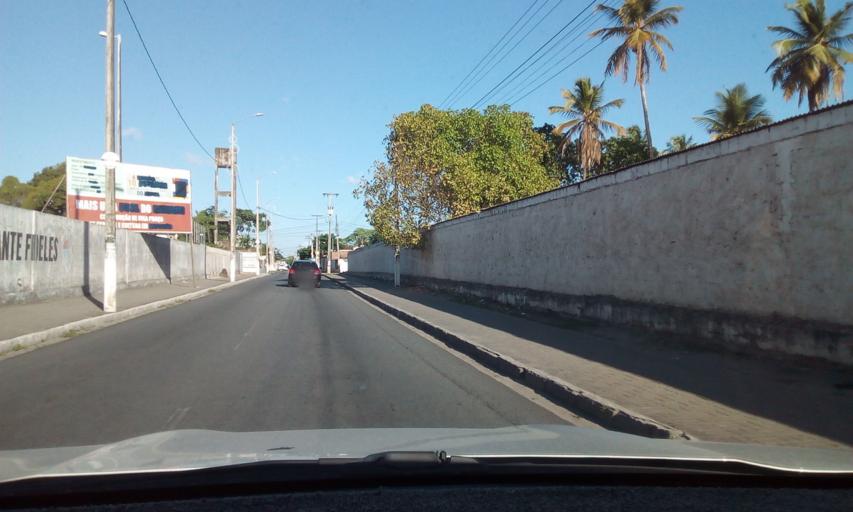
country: BR
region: Paraiba
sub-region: Bayeux
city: Bayeux
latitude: -7.1254
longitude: -34.9200
